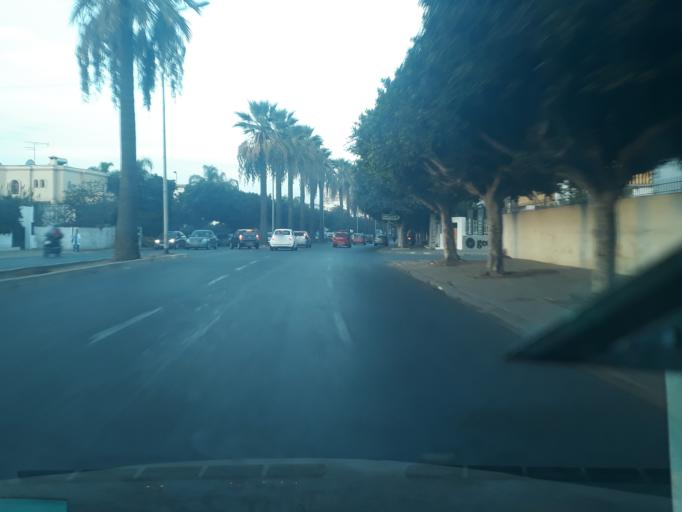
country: MA
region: Grand Casablanca
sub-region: Casablanca
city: Casablanca
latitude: 33.5810
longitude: -7.6527
